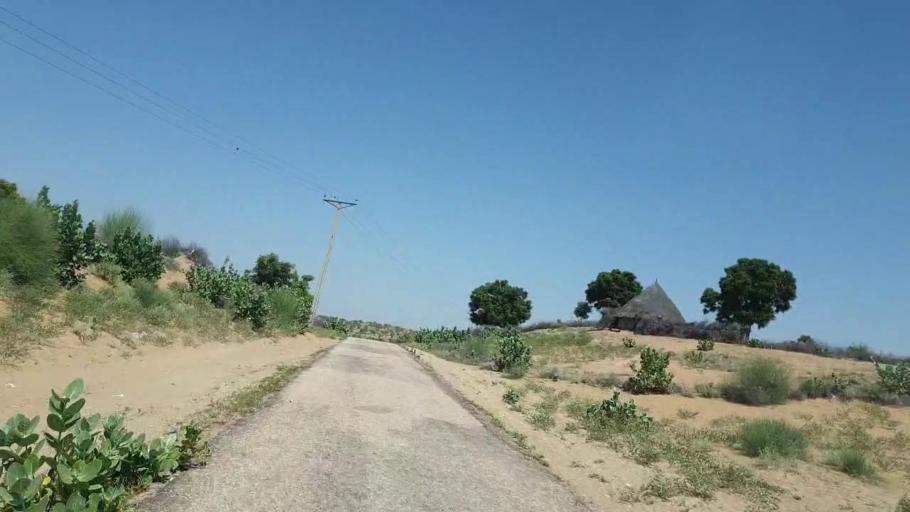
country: PK
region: Sindh
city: Islamkot
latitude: 25.1618
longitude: 70.4128
